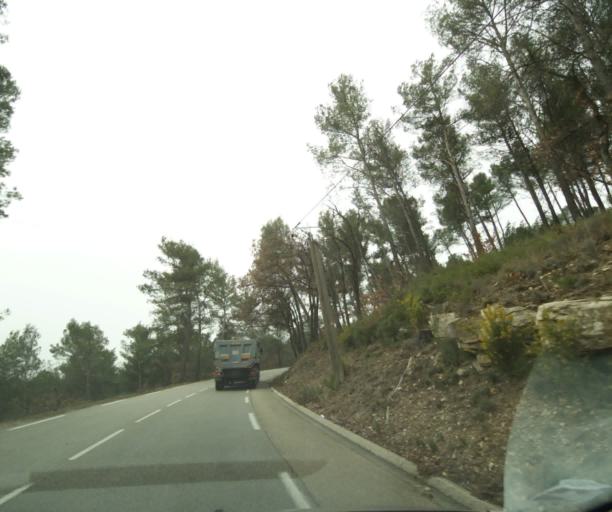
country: FR
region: Provence-Alpes-Cote d'Azur
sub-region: Departement des Bouches-du-Rhone
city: Peynier
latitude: 43.4360
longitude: 5.6280
